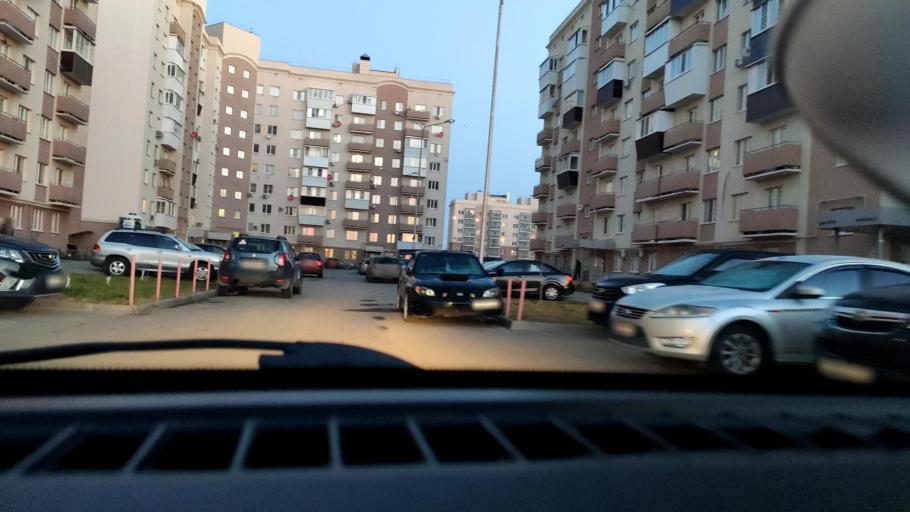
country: RU
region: Samara
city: Samara
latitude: 53.1108
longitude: 50.1452
